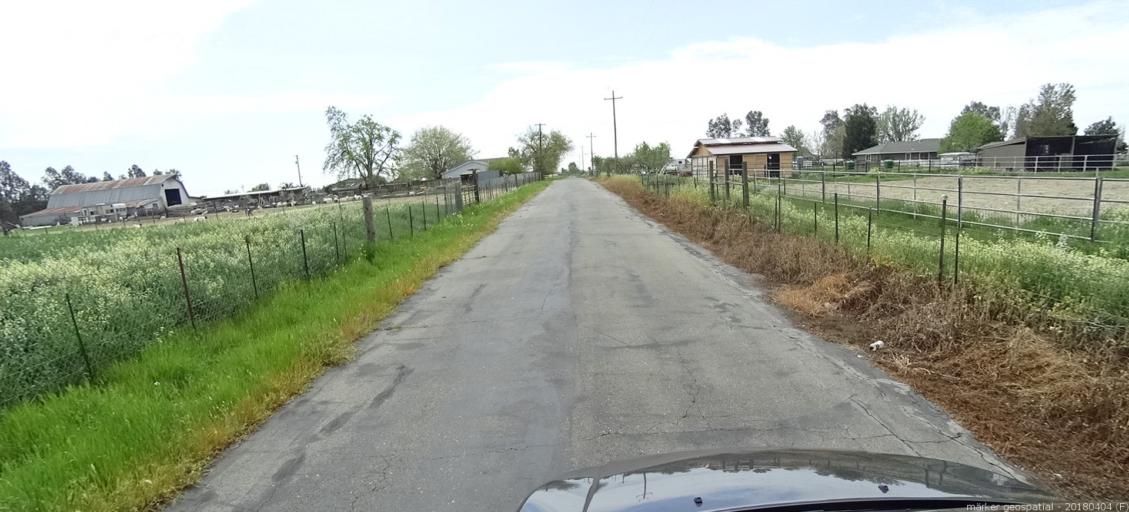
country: US
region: California
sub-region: Sacramento County
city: Herald
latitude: 38.2787
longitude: -121.2312
